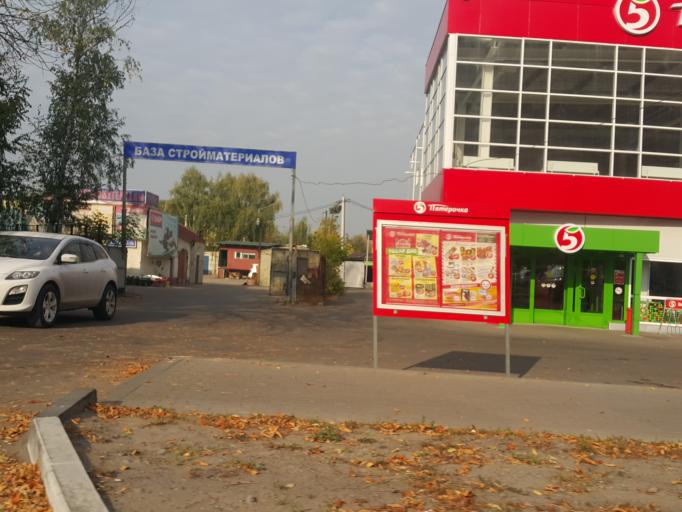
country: RU
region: Tambov
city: Tambov
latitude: 52.7013
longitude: 41.4639
